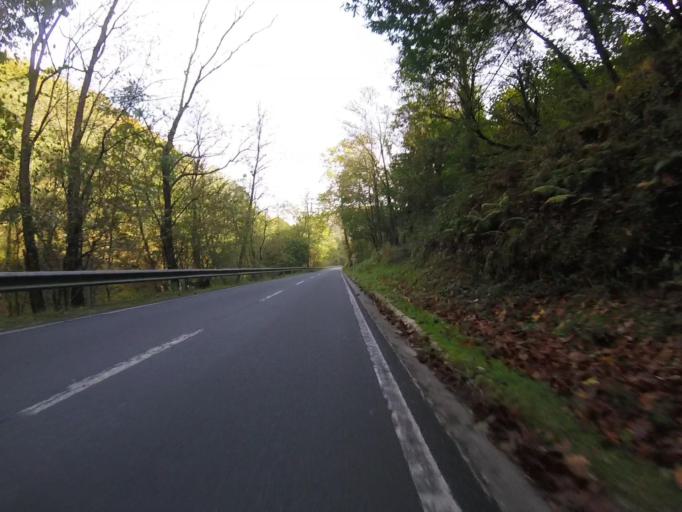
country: ES
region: Navarre
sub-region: Provincia de Navarra
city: Goizueta
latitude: 43.1841
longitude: -1.8594
